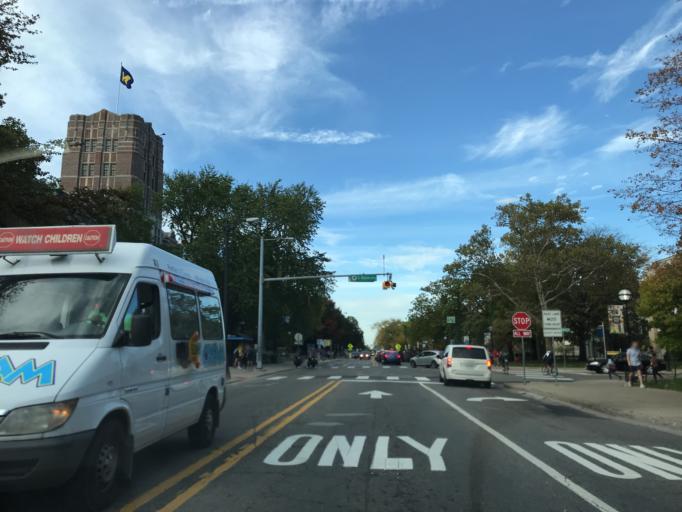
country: US
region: Michigan
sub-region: Washtenaw County
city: Ann Arbor
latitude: 42.2745
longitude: -83.7407
